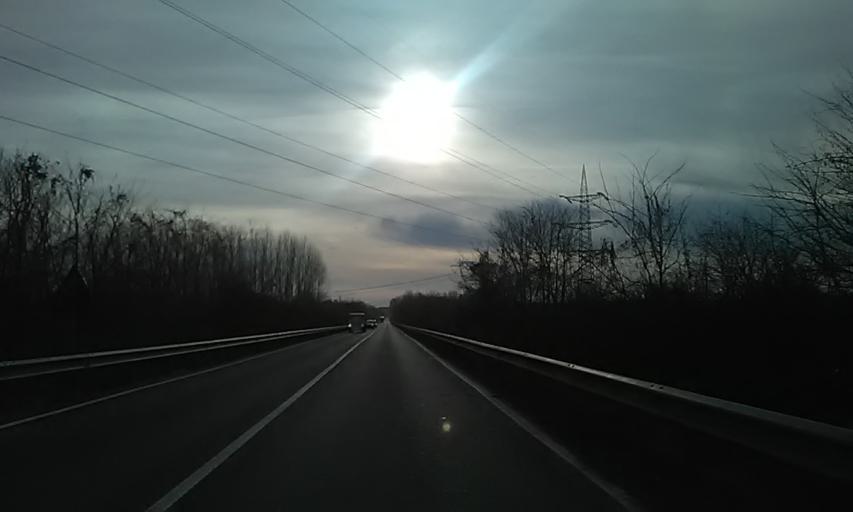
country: IT
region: Piedmont
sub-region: Provincia di Torino
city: Rondissone
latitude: 45.2630
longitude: 7.9747
